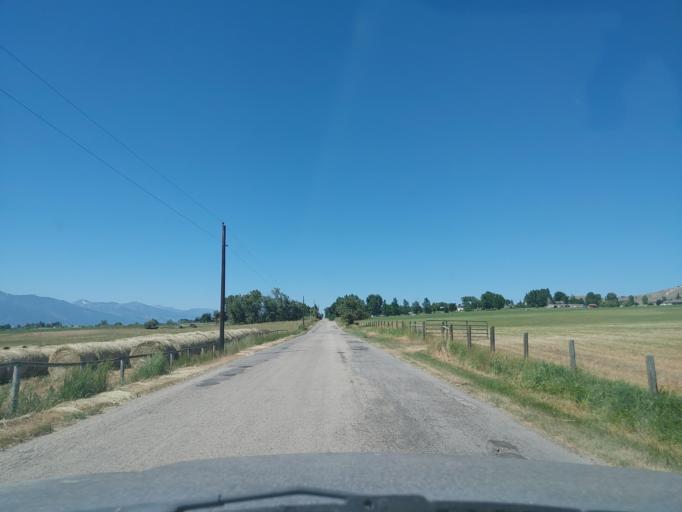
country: US
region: Montana
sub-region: Ravalli County
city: Hamilton
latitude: 46.3172
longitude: -114.0613
